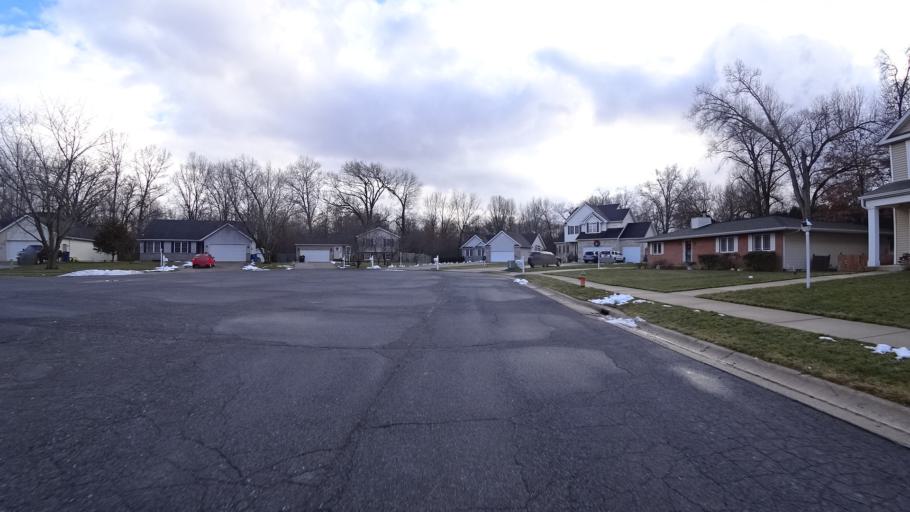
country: US
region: Indiana
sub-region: Porter County
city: Porter
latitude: 41.6068
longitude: -87.0860
